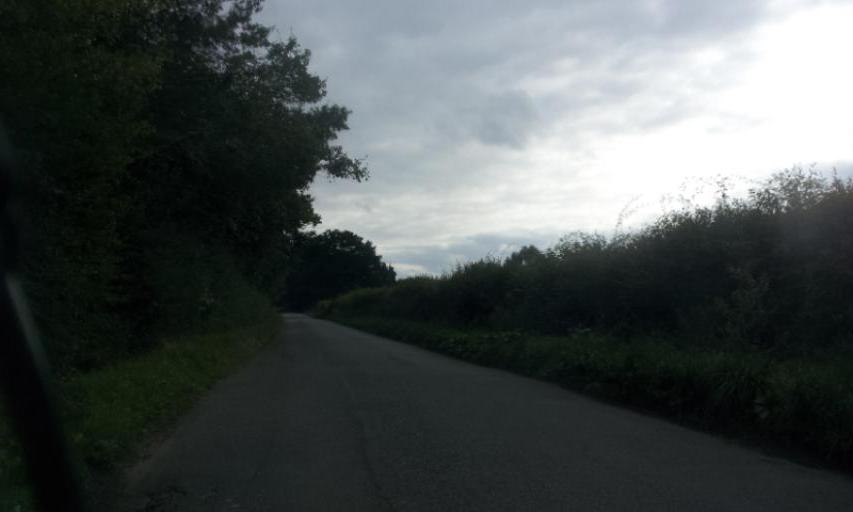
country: GB
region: England
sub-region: Kent
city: Hadlow
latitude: 51.2449
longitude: 0.3040
